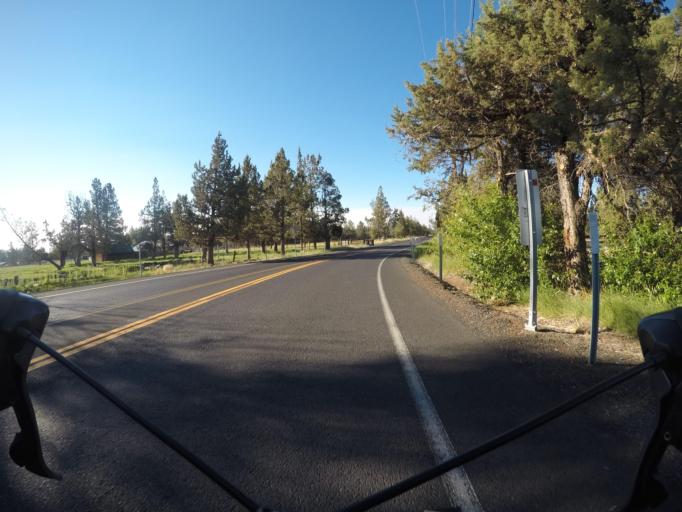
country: US
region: Oregon
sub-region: Deschutes County
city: Redmond
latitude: 44.2094
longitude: -121.2436
